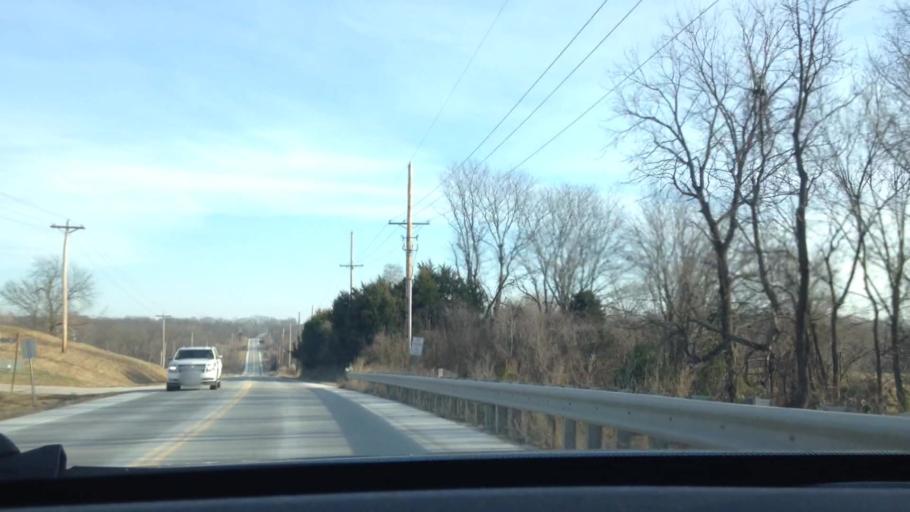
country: US
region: Missouri
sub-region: Platte County
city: Weston
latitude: 39.4144
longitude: -94.8868
